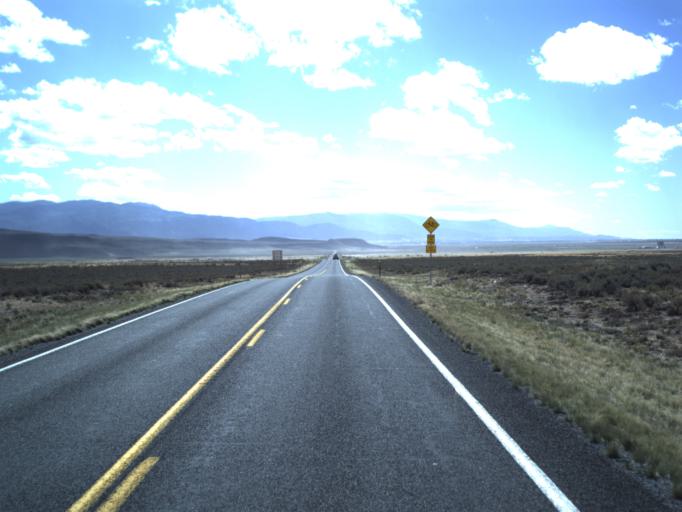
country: US
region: Utah
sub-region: Iron County
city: Enoch
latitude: 37.9106
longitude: -113.0316
